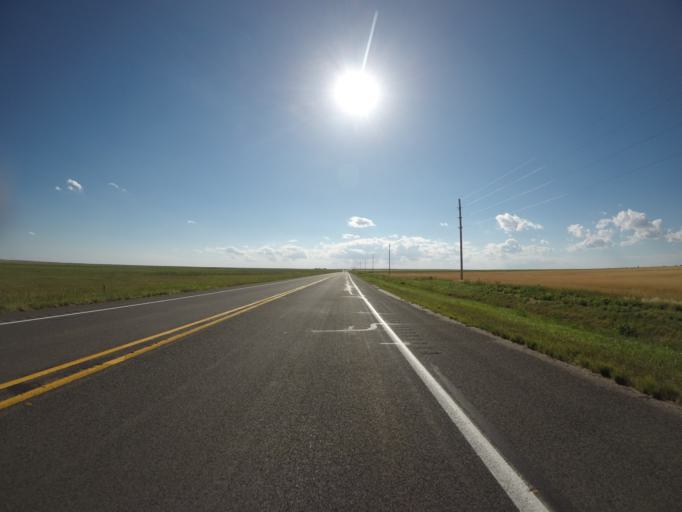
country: US
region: Colorado
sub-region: Morgan County
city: Brush
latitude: 40.6099
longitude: -103.6839
